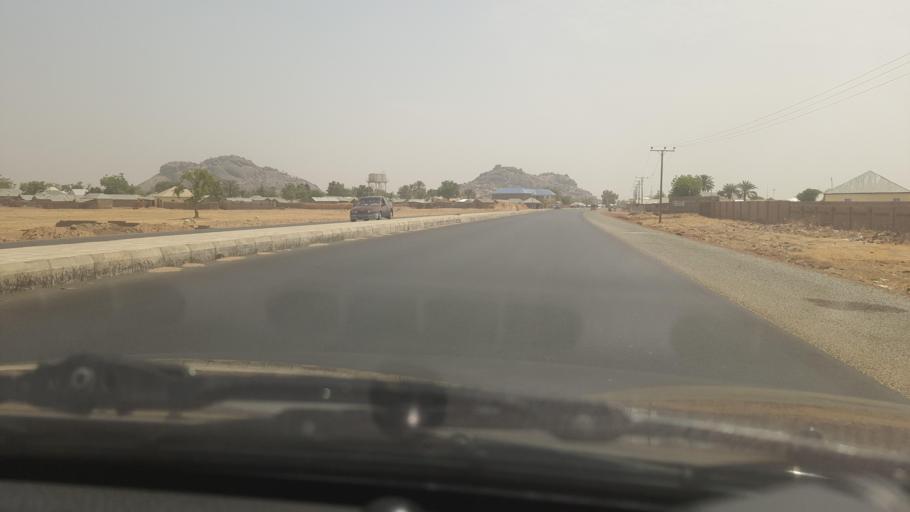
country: NG
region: Bauchi
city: Bauchi
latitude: 10.3012
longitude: 9.7388
